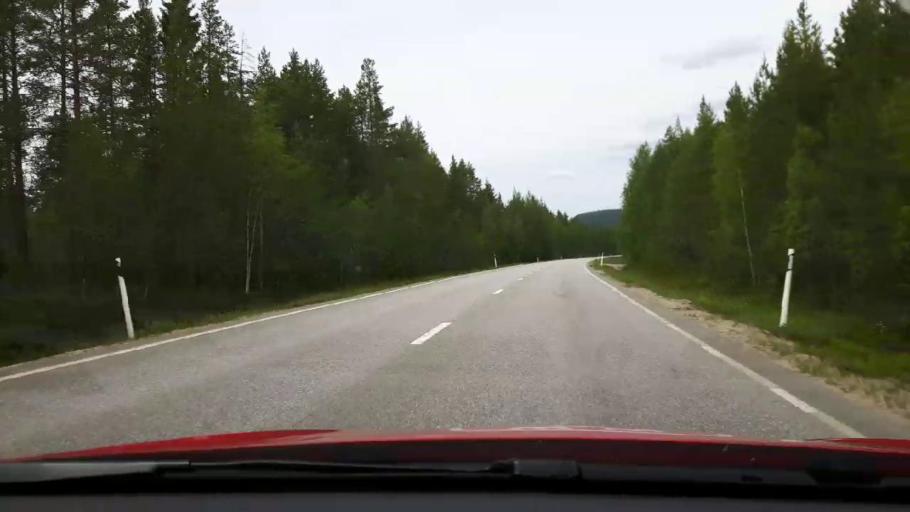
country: SE
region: Jaemtland
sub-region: Harjedalens Kommun
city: Sveg
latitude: 62.0803
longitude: 14.2589
